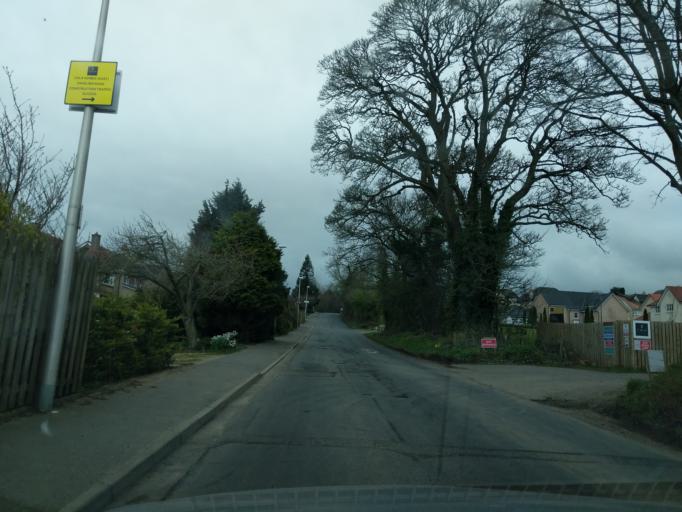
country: GB
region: Scotland
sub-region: Edinburgh
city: Balerno
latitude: 55.8903
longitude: -3.3460
